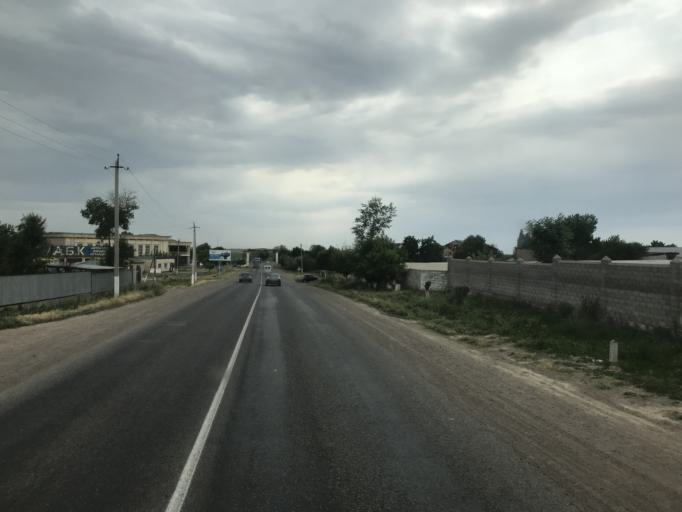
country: KZ
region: Ongtustik Qazaqstan
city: Saryaghash
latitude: 41.3720
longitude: 68.9974
